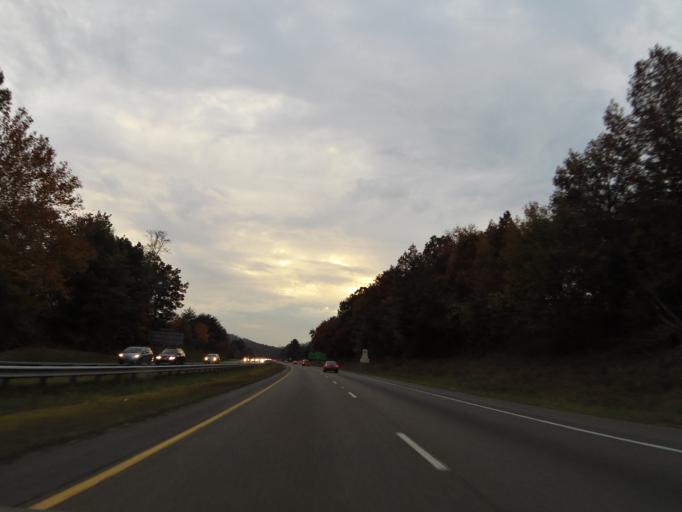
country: US
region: North Carolina
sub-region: Burke County
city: Rutherford College
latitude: 35.7321
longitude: -81.5393
